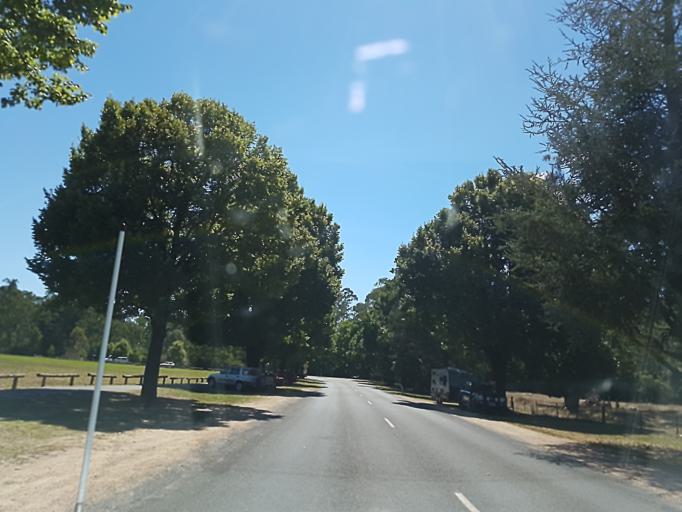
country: AU
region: Victoria
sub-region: Alpine
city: Mount Beauty
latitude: -36.7455
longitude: 146.9792
